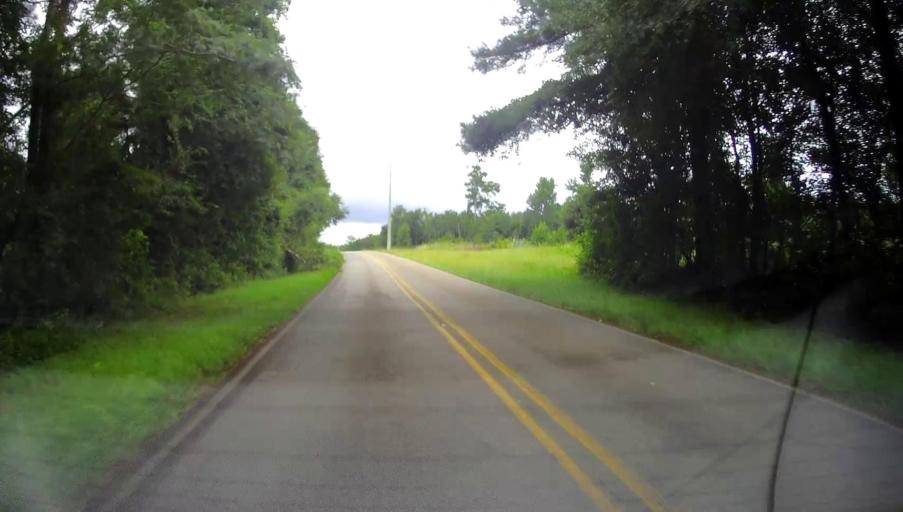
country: US
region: Georgia
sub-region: Bibb County
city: Macon
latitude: 32.7890
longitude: -83.5148
